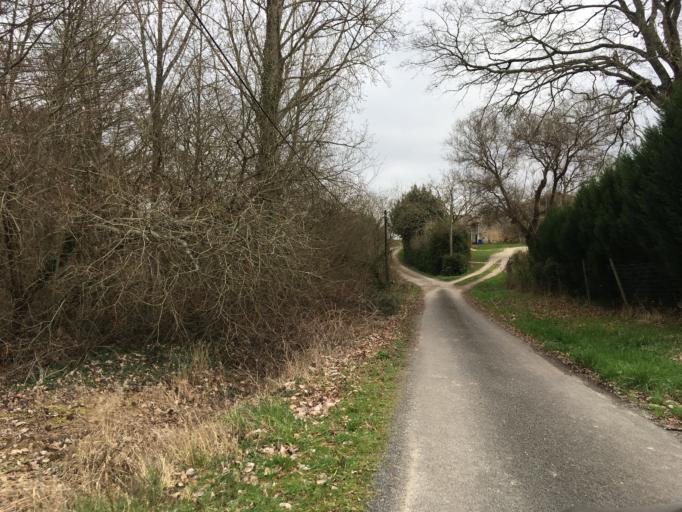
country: FR
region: Aquitaine
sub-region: Departement de la Gironde
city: Saint-Ciers-sur-Gironde
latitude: 45.3224
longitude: -0.5929
